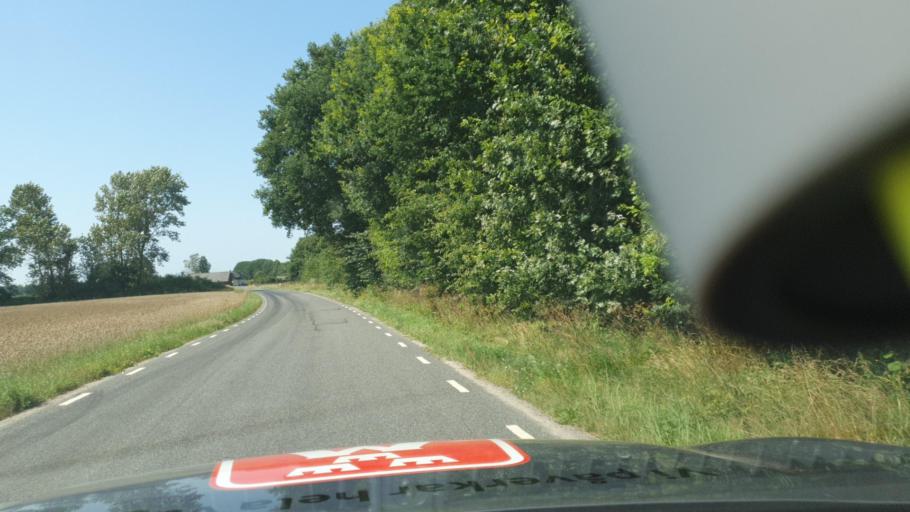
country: SE
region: Skane
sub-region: Bromolla Kommun
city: Bromoella
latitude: 56.0504
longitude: 14.3873
